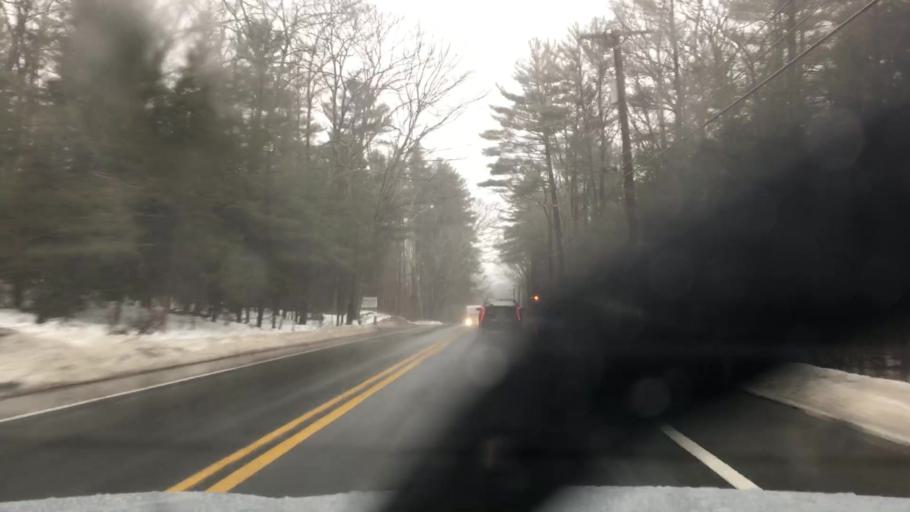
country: US
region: Massachusetts
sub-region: Franklin County
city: Shutesbury
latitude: 42.4869
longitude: -72.3415
